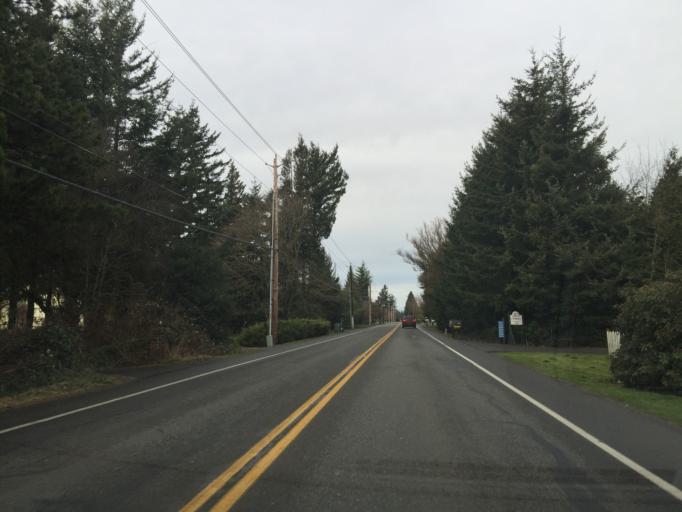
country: US
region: Washington
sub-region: Whatcom County
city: Ferndale
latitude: 48.8390
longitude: -122.5409
